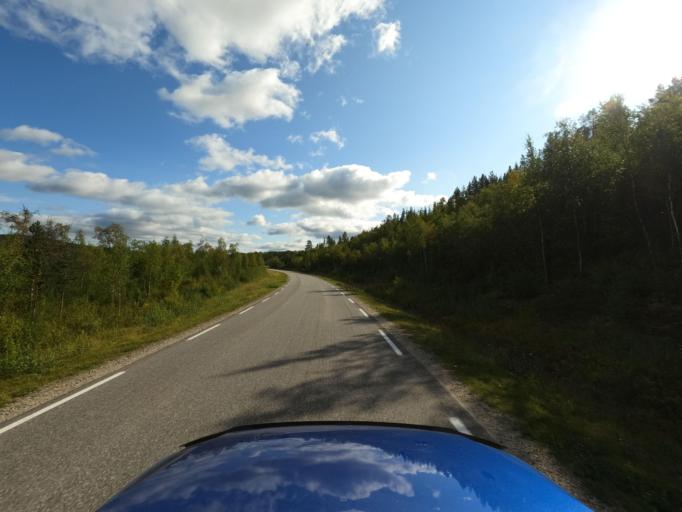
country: NO
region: Finnmark Fylke
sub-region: Karasjok
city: Karasjohka
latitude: 69.4493
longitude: 25.5881
